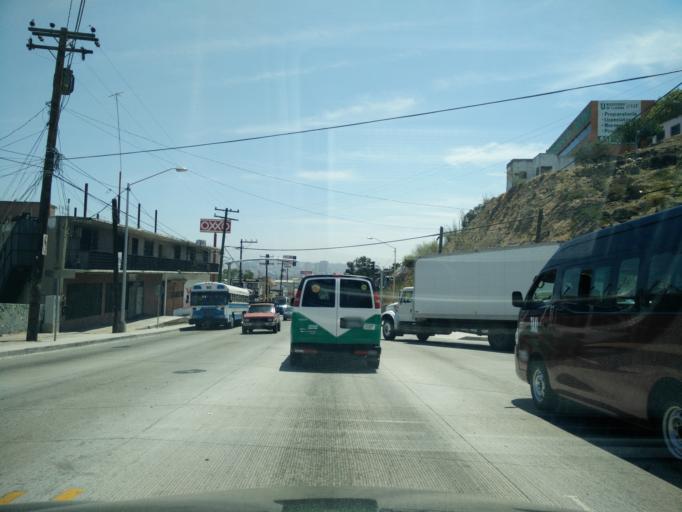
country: MX
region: Baja California
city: Tijuana
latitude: 32.5339
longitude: -117.0544
